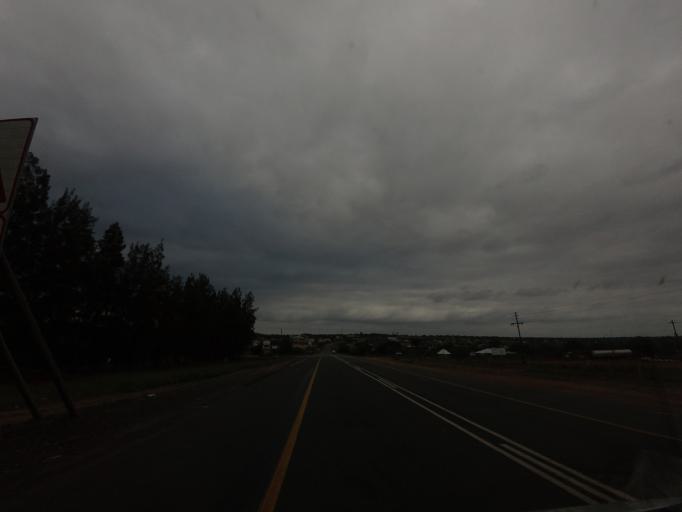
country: ZA
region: Mpumalanga
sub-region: Ehlanzeni District
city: Komatipoort
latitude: -25.4475
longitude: 31.6711
